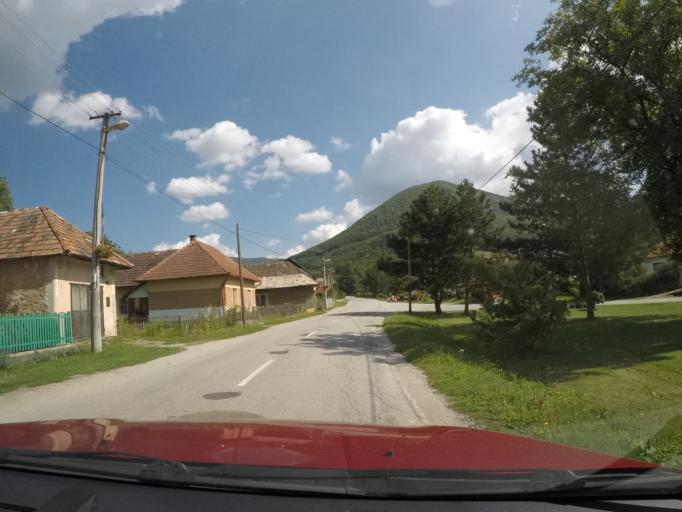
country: SK
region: Kosicky
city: Roznava
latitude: 48.6405
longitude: 20.6540
